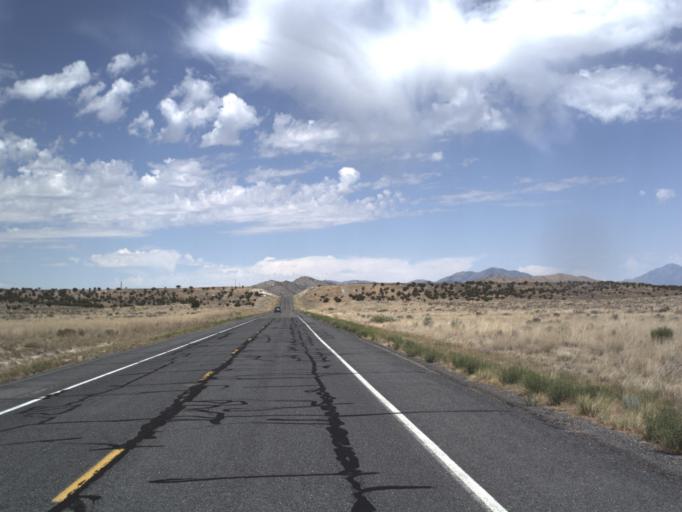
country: US
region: Utah
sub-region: Utah County
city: Eagle Mountain
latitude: 40.0613
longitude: -112.3138
